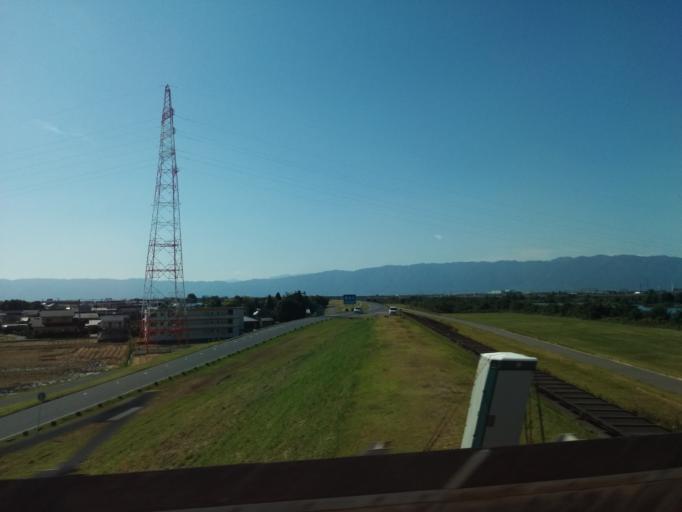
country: JP
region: Gifu
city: Ogaki
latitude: 35.3218
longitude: 136.6786
